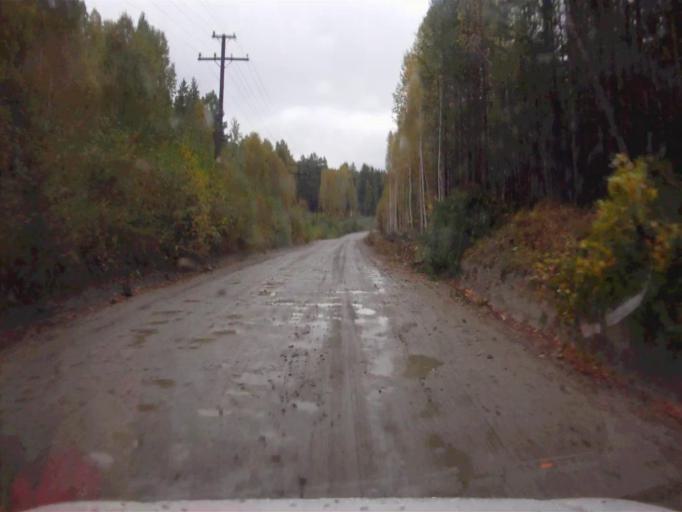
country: RU
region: Chelyabinsk
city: Kyshtym
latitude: 55.7989
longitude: 60.4805
